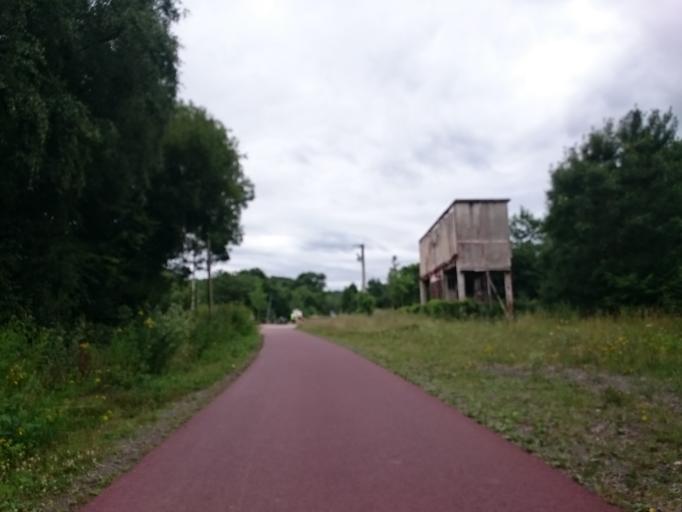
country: FR
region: Lower Normandy
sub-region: Departement du Calvados
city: Saint-Andre-sur-Orne
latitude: 49.1072
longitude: -0.3854
